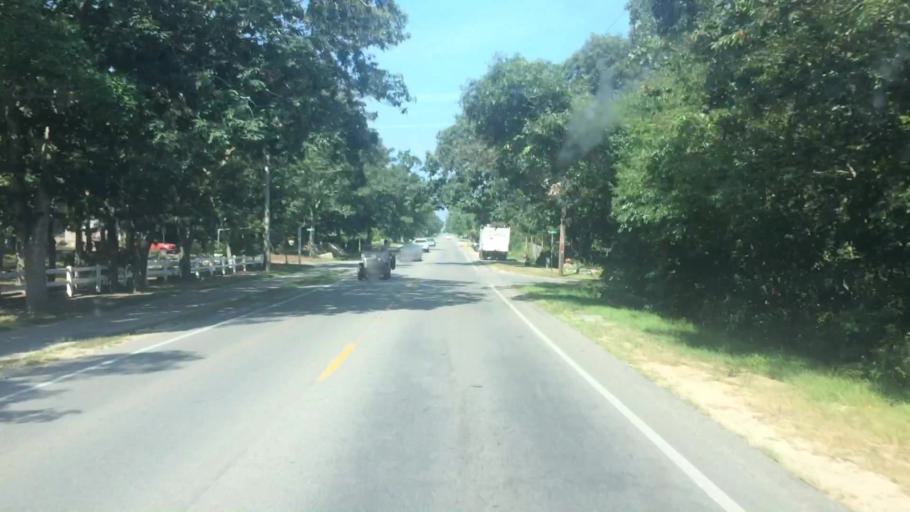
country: US
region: Massachusetts
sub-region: Dukes County
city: Edgartown
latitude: 41.4014
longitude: -70.5520
